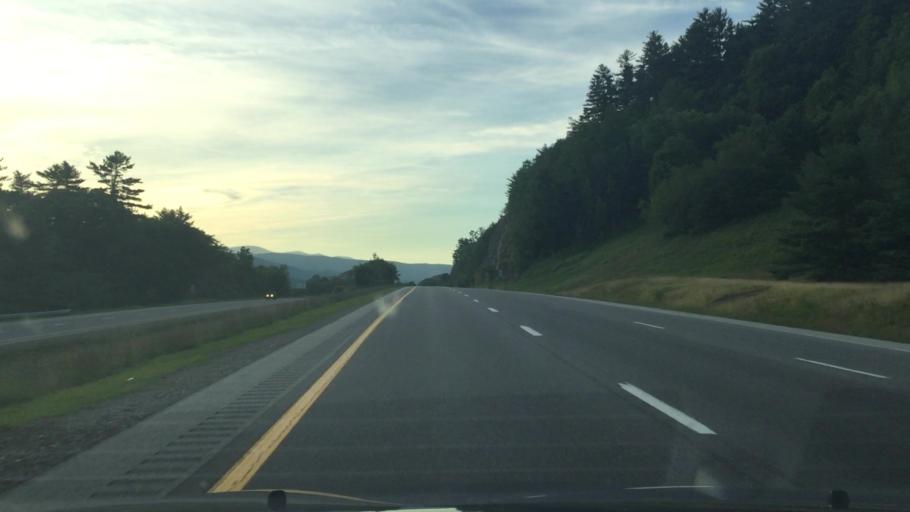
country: US
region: New Hampshire
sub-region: Grafton County
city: Thornton
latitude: 43.8549
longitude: -71.6487
